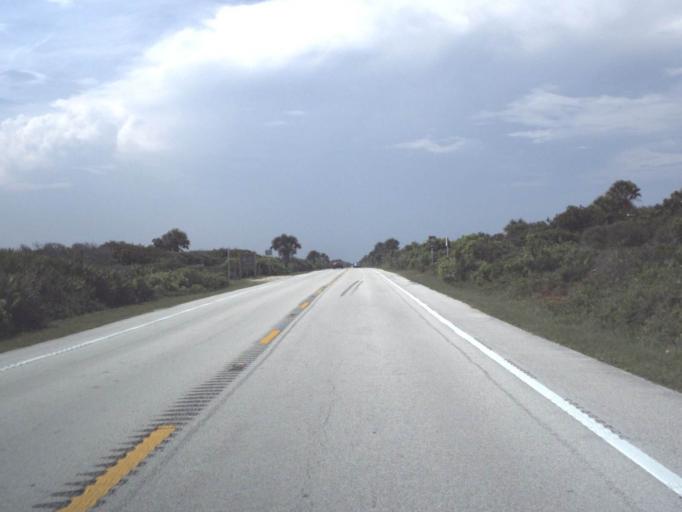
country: US
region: Florida
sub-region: Saint Johns County
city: Palm Valley
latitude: 30.1095
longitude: -81.3439
